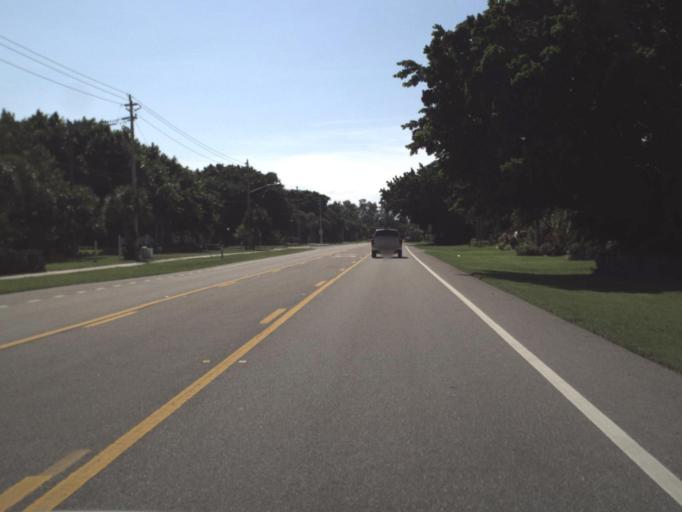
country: US
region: Florida
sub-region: Manatee County
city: Longboat Key
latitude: 27.3934
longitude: -82.6440
